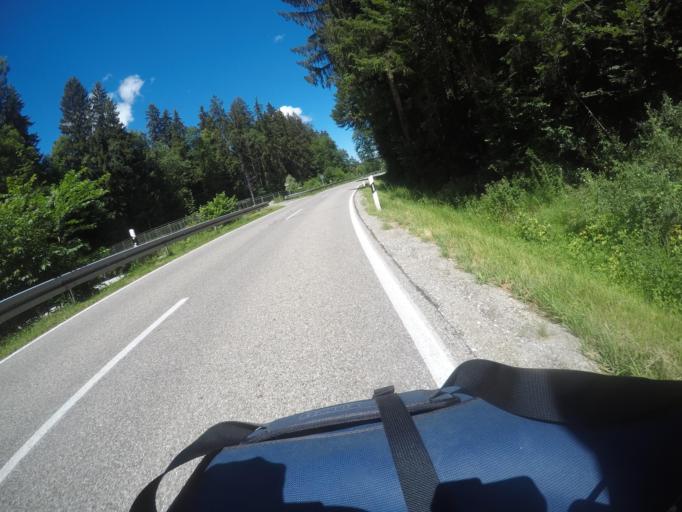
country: DE
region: Bavaria
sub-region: Upper Bavaria
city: Prem
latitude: 47.6544
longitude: 10.7876
